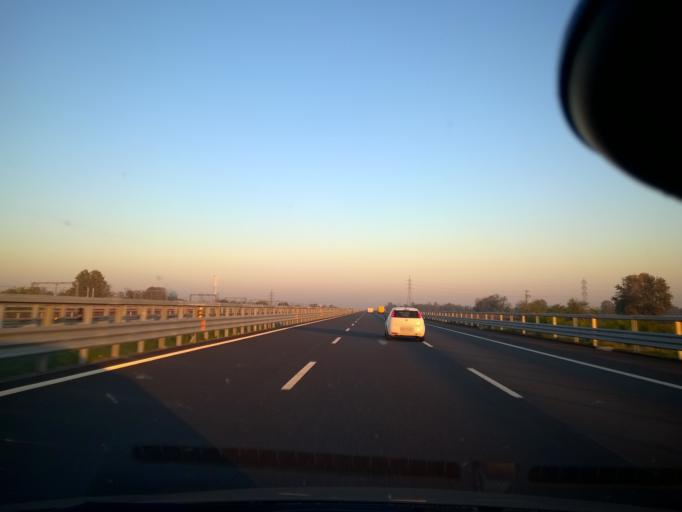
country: IT
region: Lombardy
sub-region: Citta metropolitana di Milano
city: Trecella
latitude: 45.5070
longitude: 9.4714
